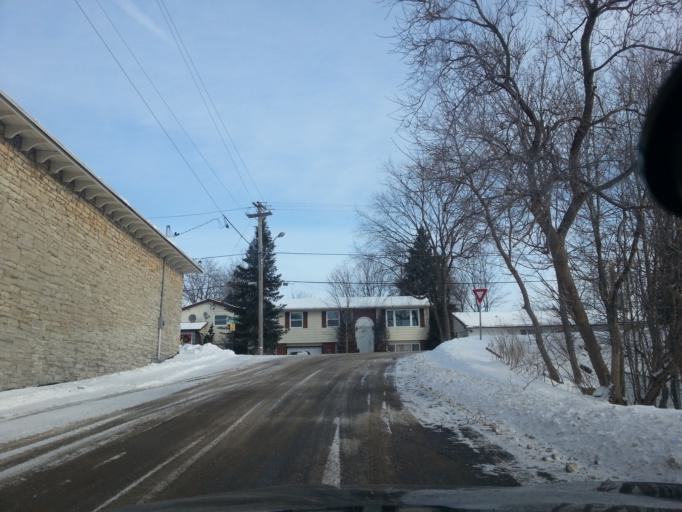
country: CA
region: Ontario
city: Carleton Place
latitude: 45.2278
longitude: -76.1998
